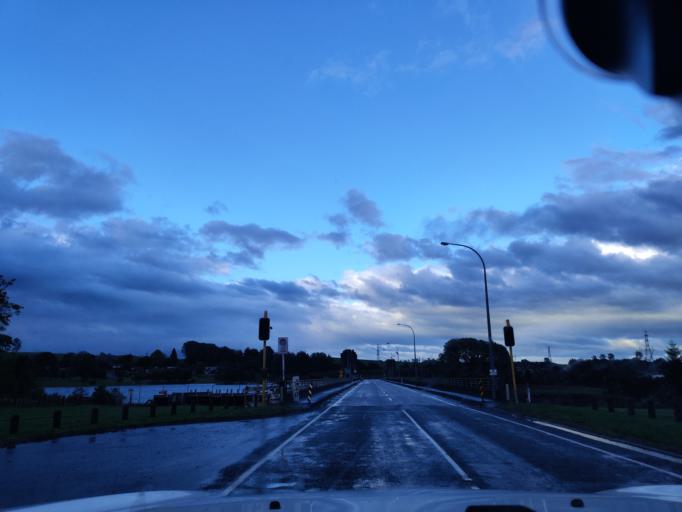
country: NZ
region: Waikato
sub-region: South Waikato District
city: Tokoroa
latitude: -38.4190
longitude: 175.8098
